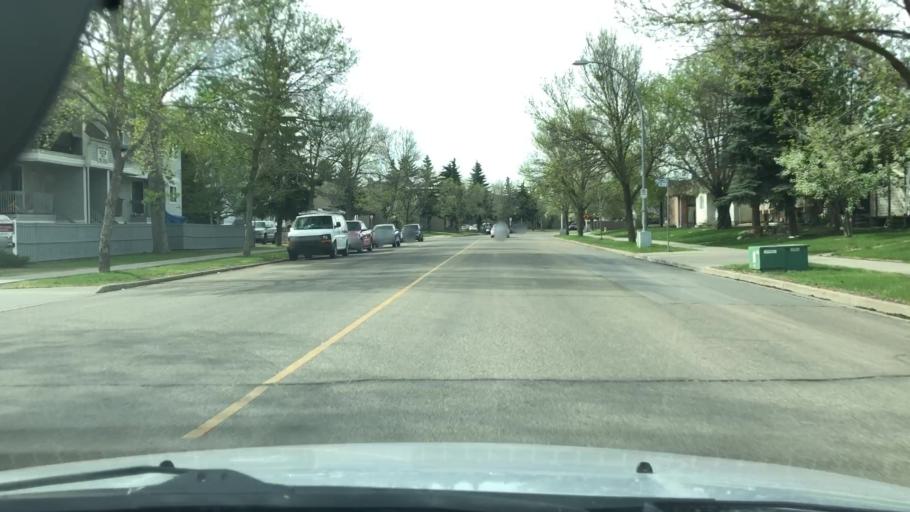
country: CA
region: Alberta
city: Edmonton
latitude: 53.6016
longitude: -113.5285
